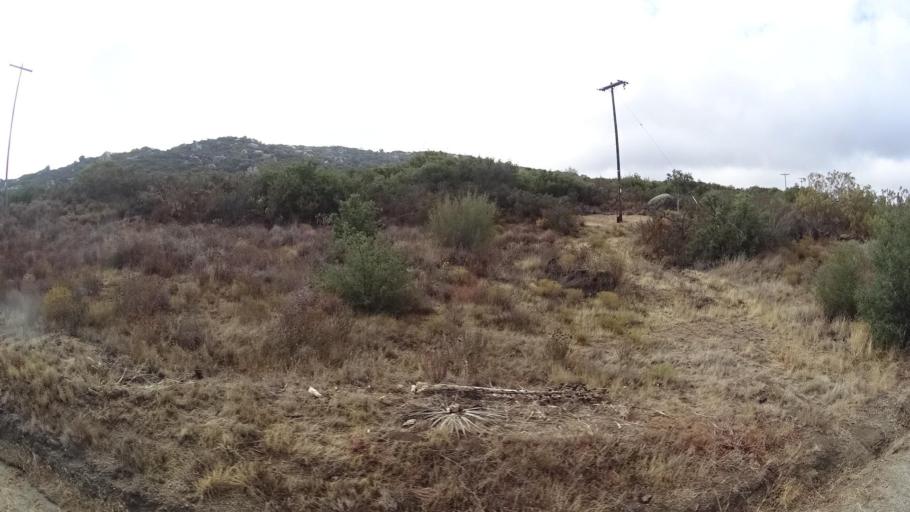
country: MX
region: Baja California
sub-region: Tecate
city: Hacienda Tecate
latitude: 32.6189
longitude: -116.5675
